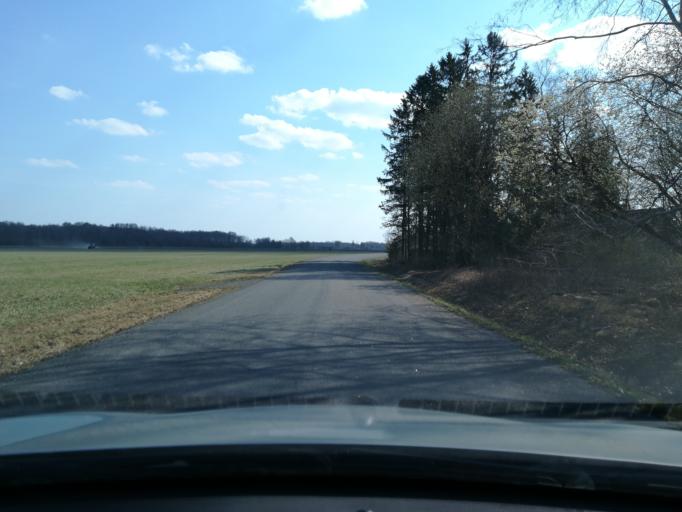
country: EE
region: Harju
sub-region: Saue linn
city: Saue
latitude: 59.3327
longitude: 24.4999
